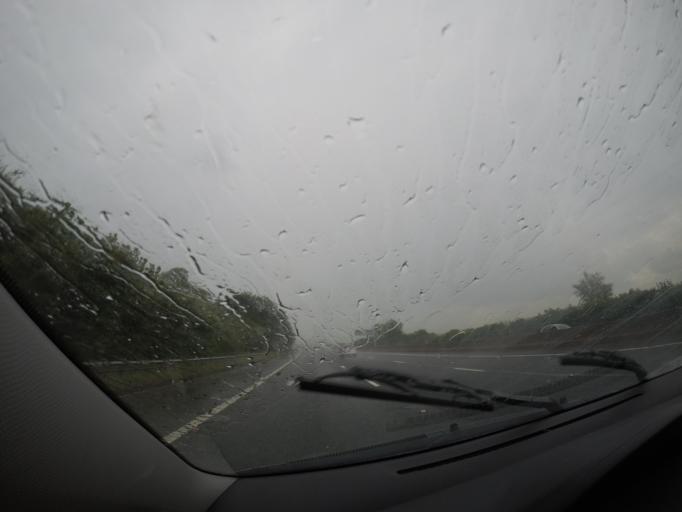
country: GB
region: England
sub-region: Cumbria
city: Penrith
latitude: 54.6696
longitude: -2.7750
